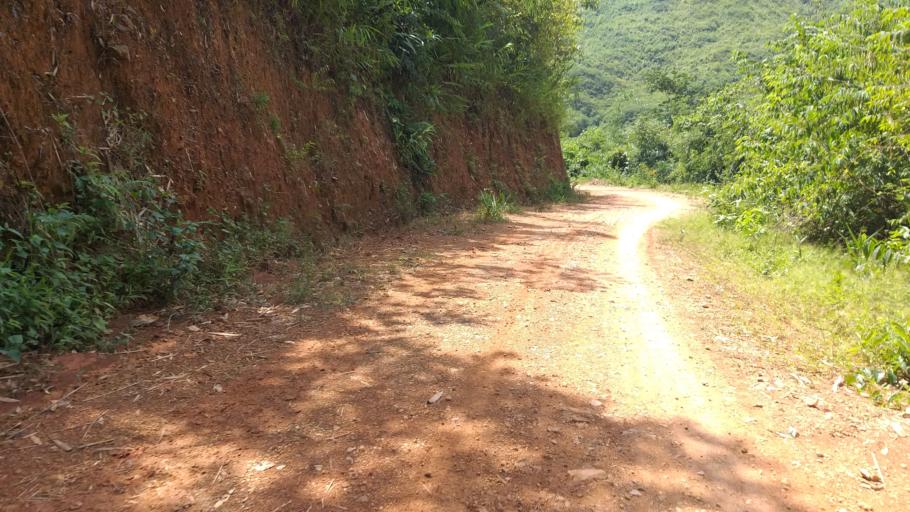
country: LA
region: Phongsali
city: Khoa
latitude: 21.3117
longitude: 102.5666
